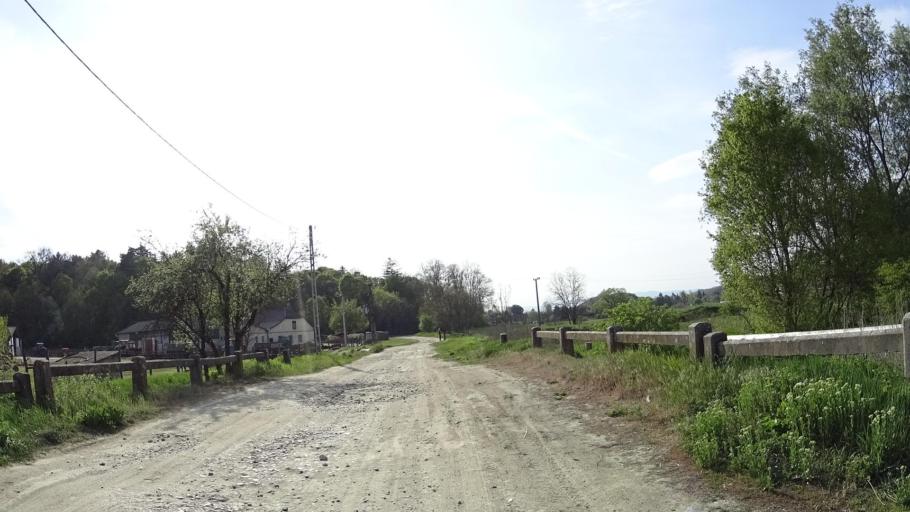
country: HU
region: Nograd
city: Romhany
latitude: 47.8849
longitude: 19.2031
